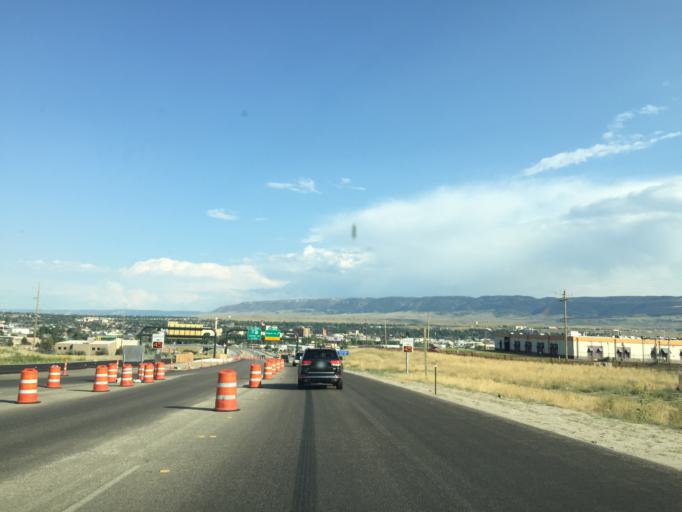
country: US
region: Wyoming
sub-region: Natrona County
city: Casper
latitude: 42.8623
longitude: -106.3406
